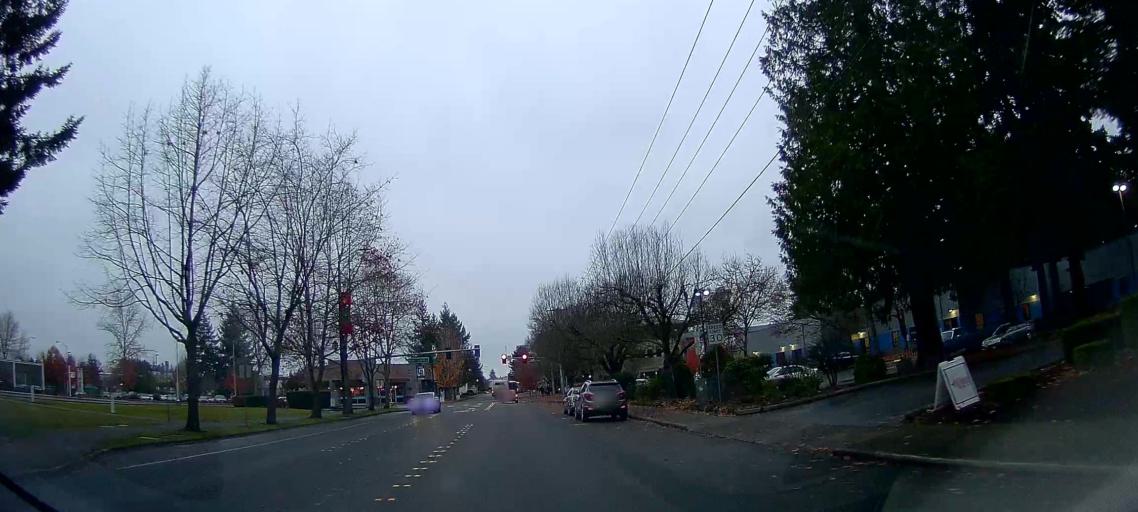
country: US
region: Washington
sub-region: Thurston County
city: Lacey
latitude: 47.0434
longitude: -122.8289
